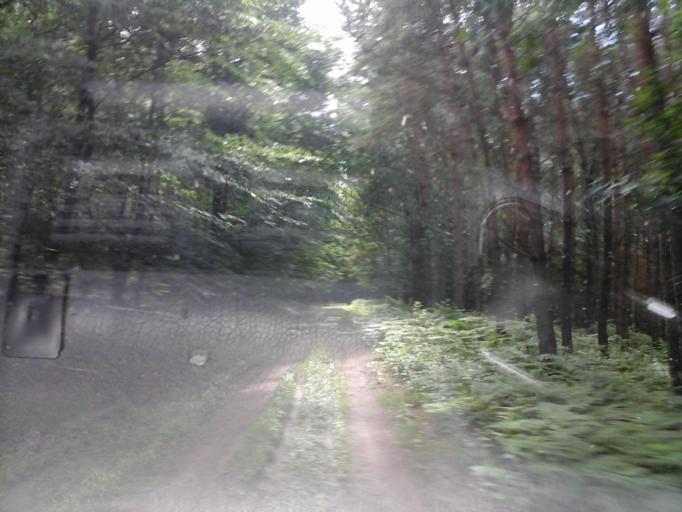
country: PL
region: West Pomeranian Voivodeship
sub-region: Powiat choszczenski
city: Bierzwnik
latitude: 52.9812
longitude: 15.6135
